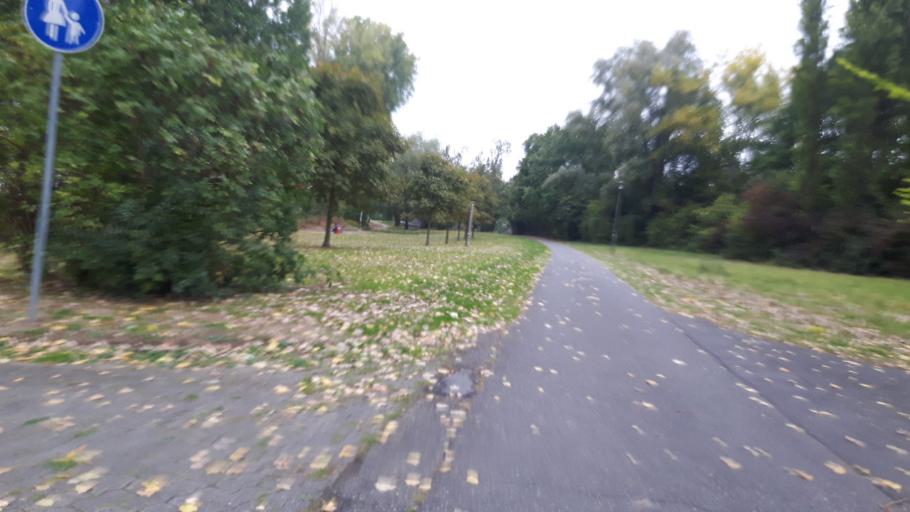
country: DE
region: North Rhine-Westphalia
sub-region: Regierungsbezirk Koln
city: Konigswinter
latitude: 50.7021
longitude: 7.1731
